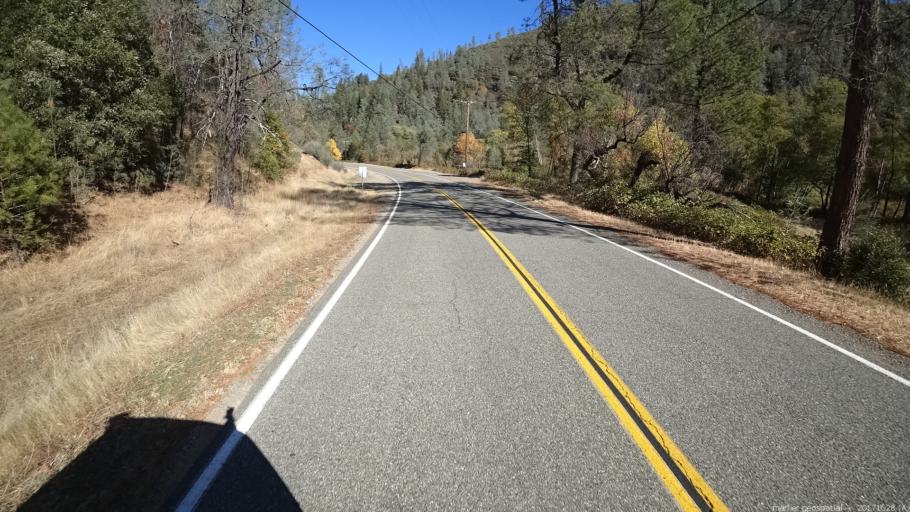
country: US
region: California
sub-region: Shasta County
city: Shasta
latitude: 40.7281
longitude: -122.6237
